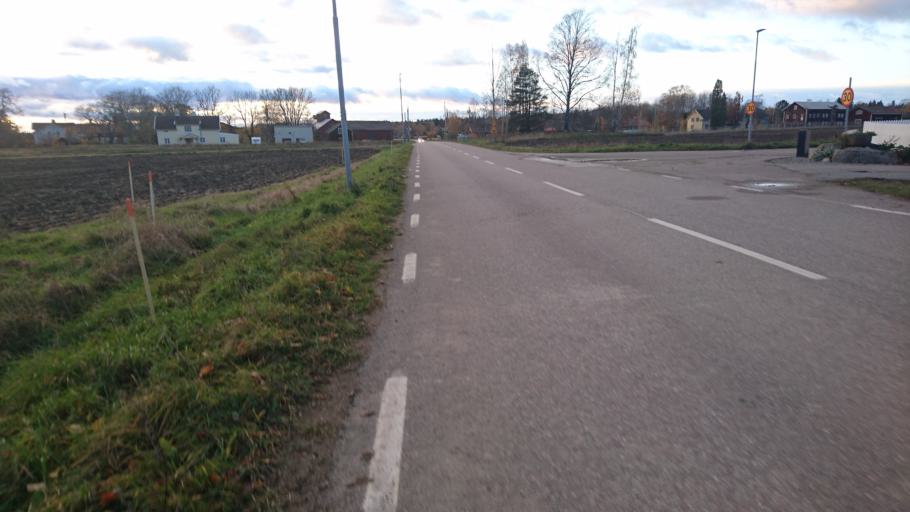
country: SE
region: Vaestmanland
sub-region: Sala Kommun
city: Sala
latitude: 59.8061
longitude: 16.6437
